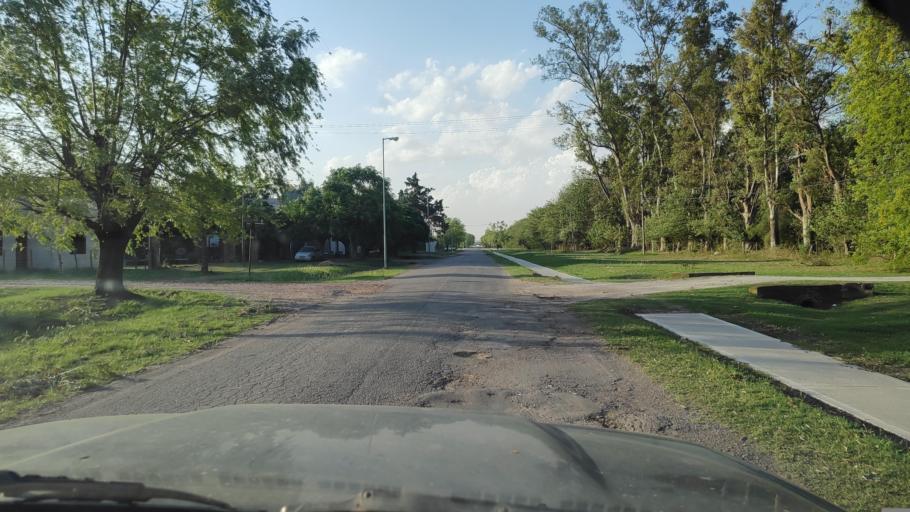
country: AR
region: Buenos Aires
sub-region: Partido de Lujan
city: Lujan
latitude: -34.5513
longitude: -59.2080
